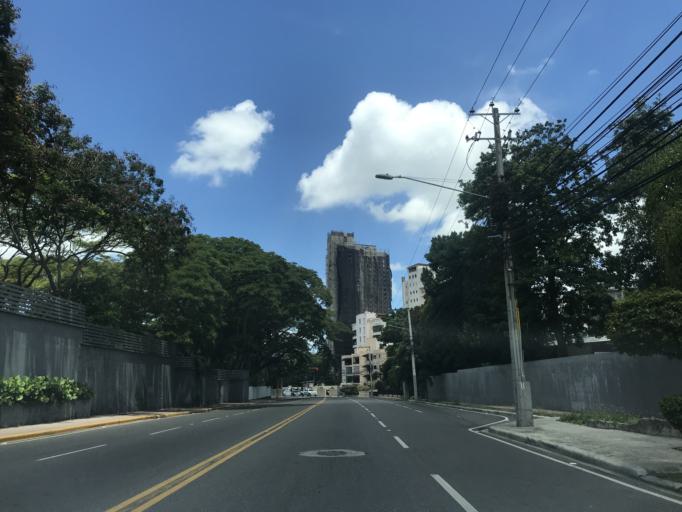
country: DO
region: Santiago
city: Santiago de los Caballeros
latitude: 19.4534
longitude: -70.6874
